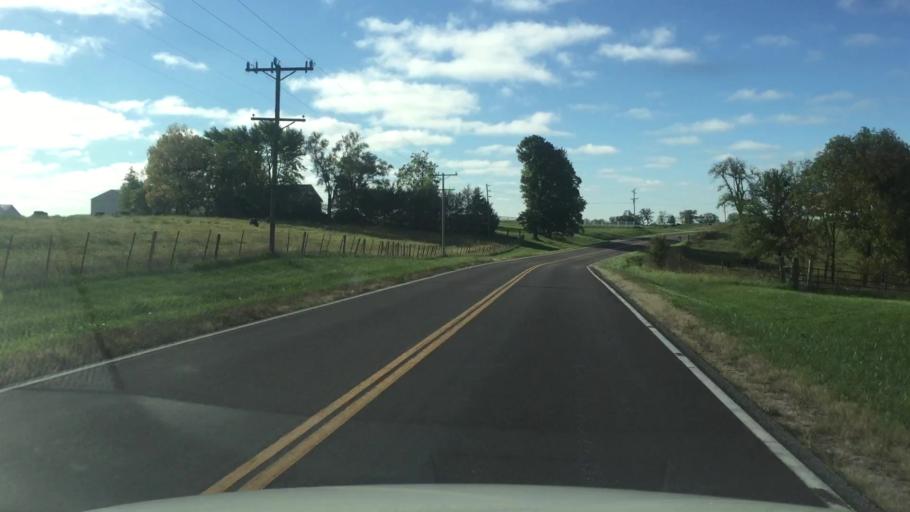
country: US
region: Missouri
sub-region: Howard County
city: New Franklin
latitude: 39.0908
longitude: -92.7434
